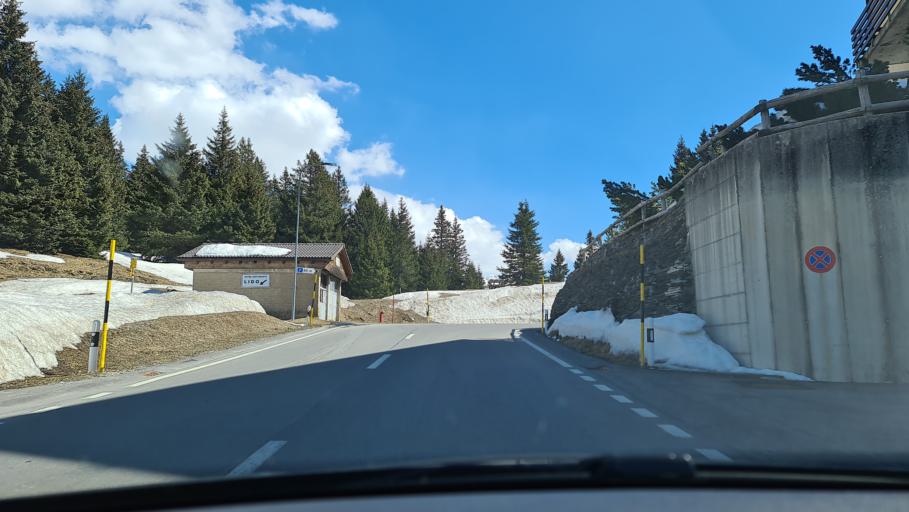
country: CH
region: Grisons
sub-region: Moesa District
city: Mesocco
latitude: 46.4481
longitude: 9.2010
